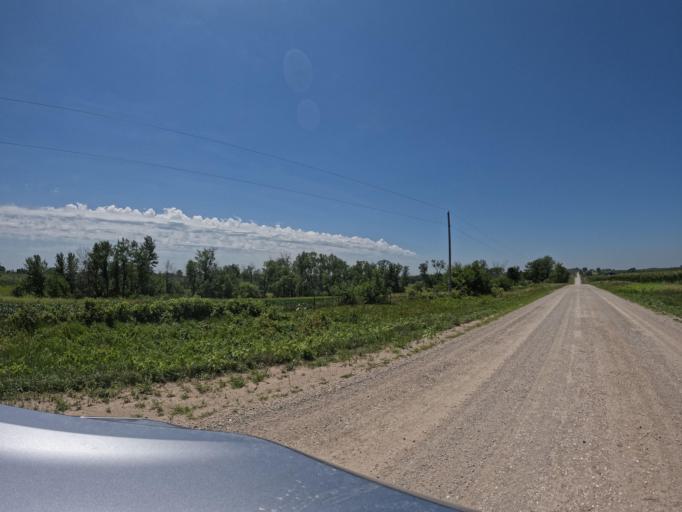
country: US
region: Iowa
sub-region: Keokuk County
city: Sigourney
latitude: 41.4090
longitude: -92.3236
